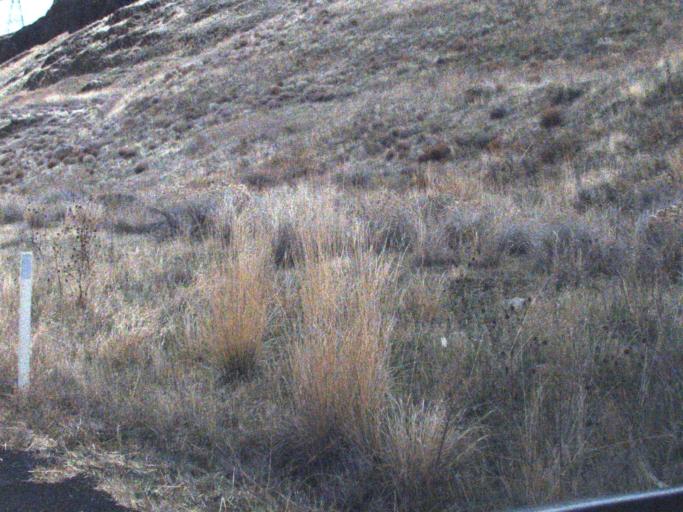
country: US
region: Washington
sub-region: Walla Walla County
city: Waitsburg
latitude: 46.5368
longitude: -118.1503
